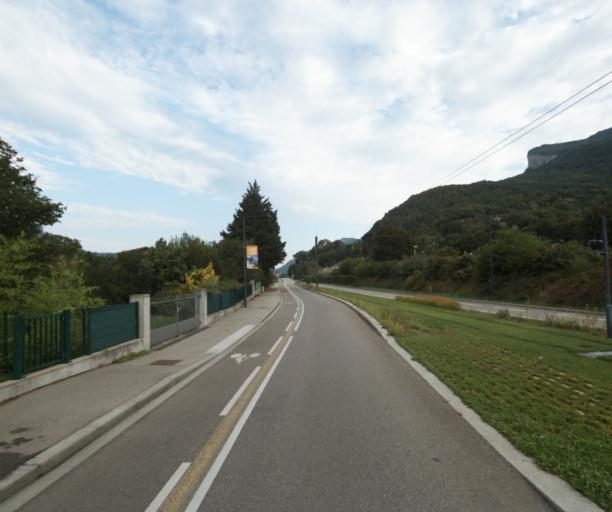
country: FR
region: Rhone-Alpes
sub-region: Departement de l'Isere
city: Fontanil-Cornillon
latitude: 45.2553
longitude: 5.6613
